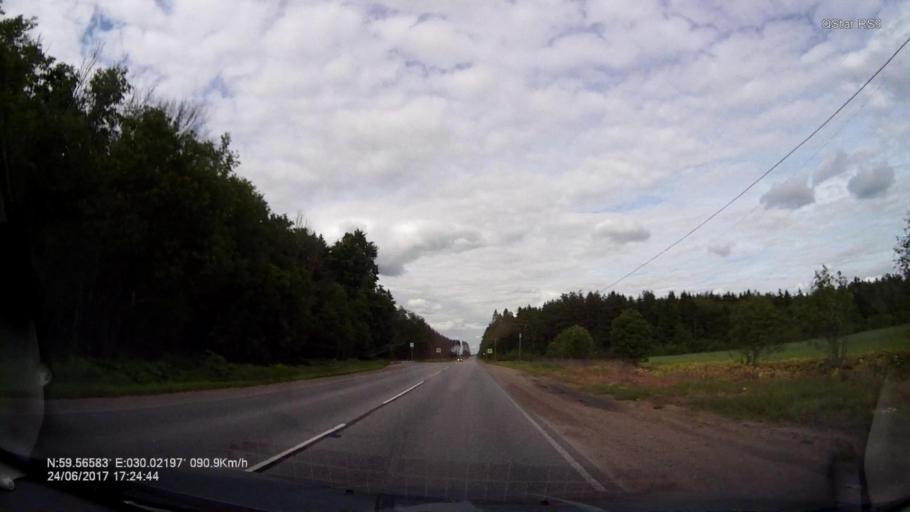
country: RU
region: Leningrad
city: Mariyenburg
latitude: 59.5660
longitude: 30.0224
